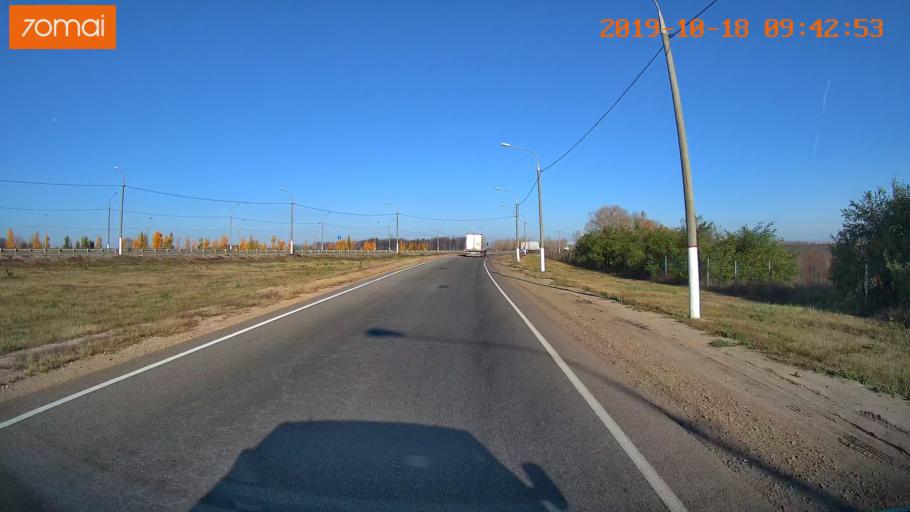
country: RU
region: Tula
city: Kazachka
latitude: 53.2909
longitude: 38.1795
